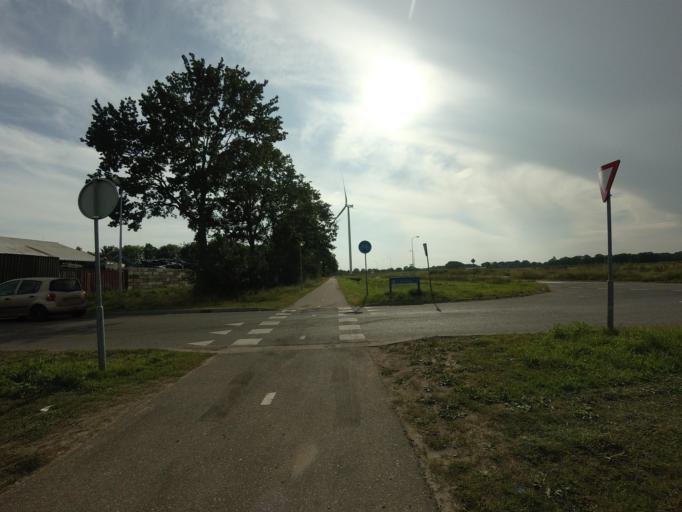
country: NL
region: Drenthe
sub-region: Gemeente Coevorden
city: Coevorden
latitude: 52.6447
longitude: 6.7177
